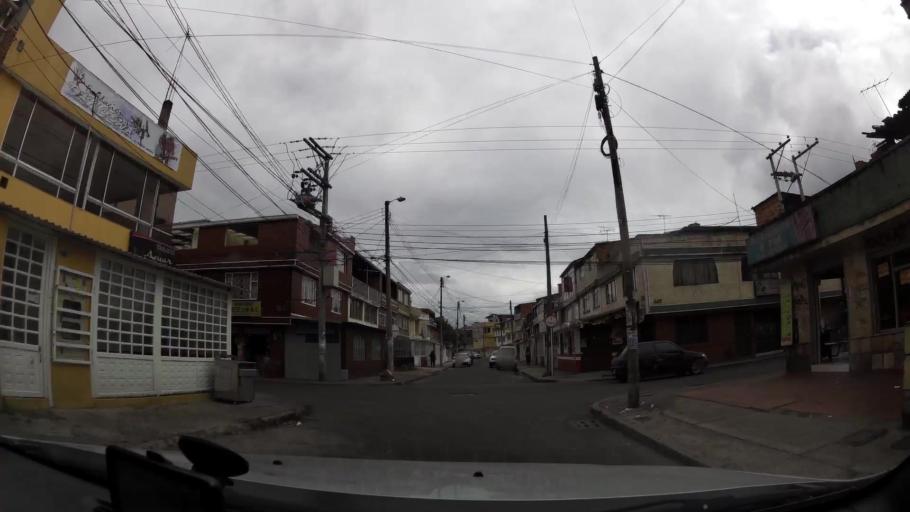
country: CO
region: Bogota D.C.
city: Bogota
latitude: 4.6199
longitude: -74.1109
